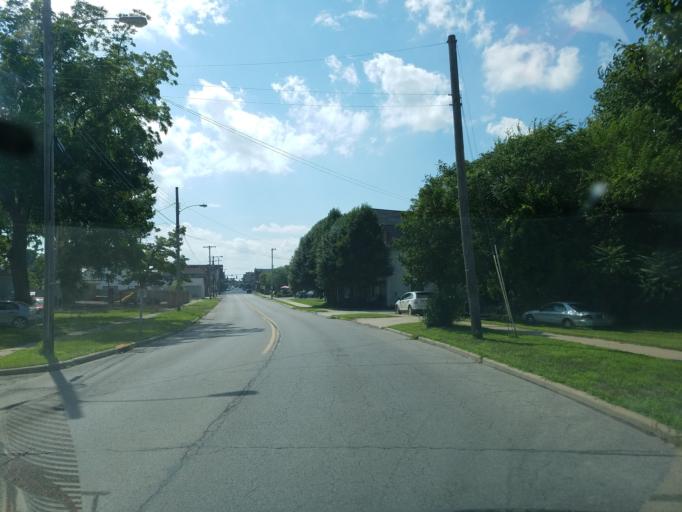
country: US
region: Ohio
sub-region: Ashland County
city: Ashland
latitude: 40.8685
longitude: -82.3097
